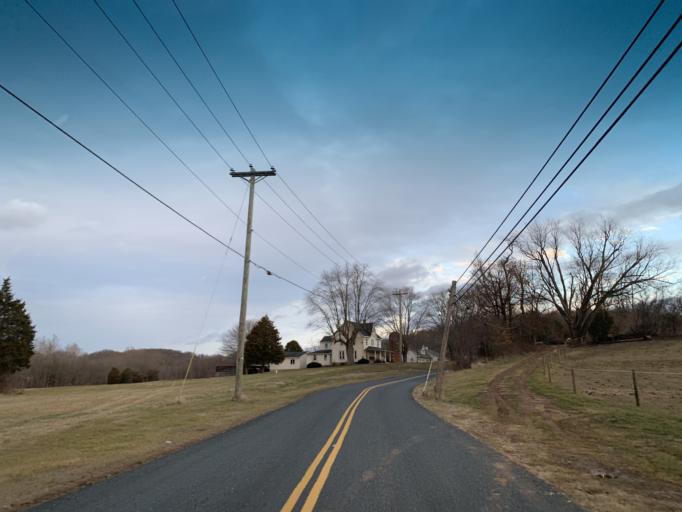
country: US
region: Pennsylvania
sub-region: York County
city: Susquehanna Trails
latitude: 39.6636
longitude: -76.3238
